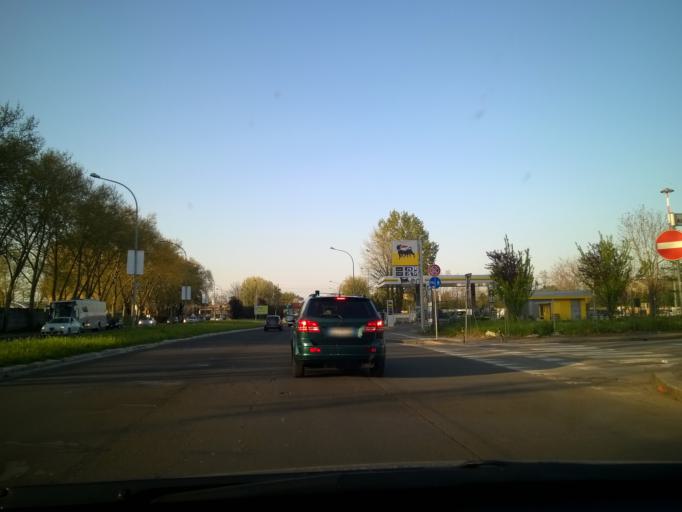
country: IT
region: Emilia-Romagna
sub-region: Provincia di Bologna
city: Bologna
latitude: 44.5167
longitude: 11.3600
